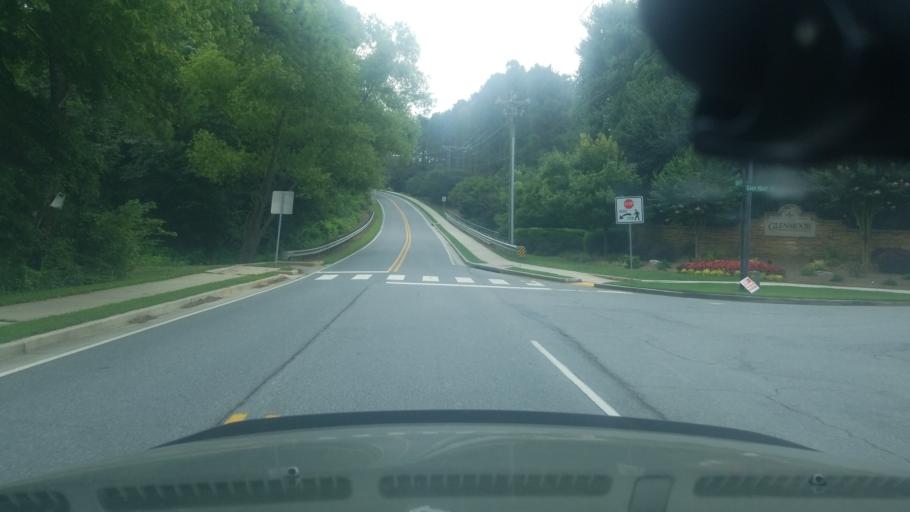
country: US
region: Georgia
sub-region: Fulton County
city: Johns Creek
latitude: 34.0975
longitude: -84.1855
